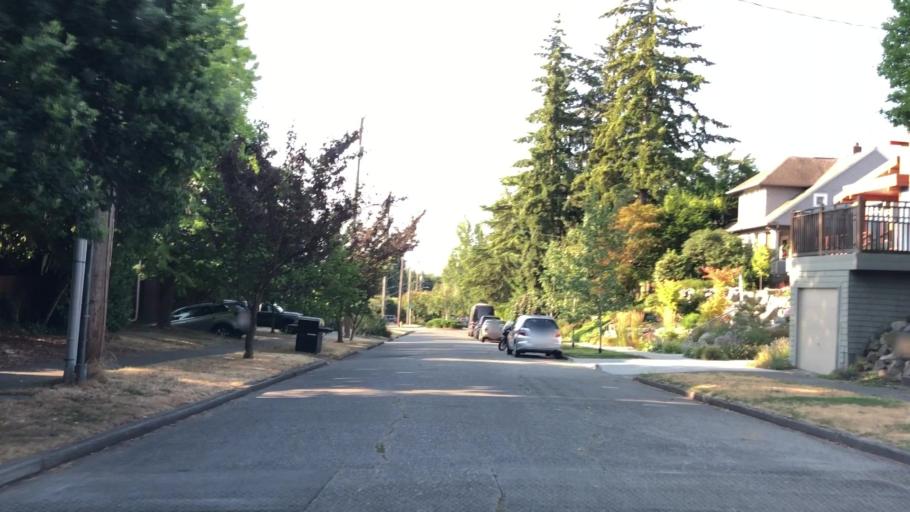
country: US
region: Washington
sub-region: King County
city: Seattle
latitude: 47.6578
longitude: -122.3338
